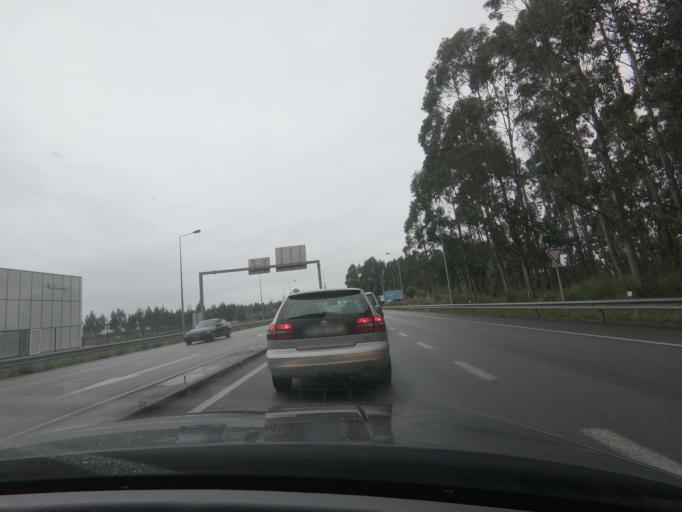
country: PT
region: Porto
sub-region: Vila do Conde
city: Arvore
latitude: 41.3037
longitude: -8.7015
